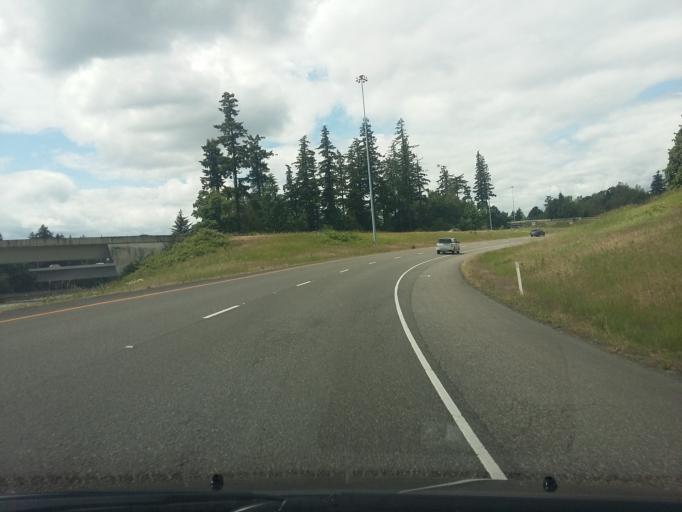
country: US
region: Washington
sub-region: Clark County
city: Orchards
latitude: 45.6032
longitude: -122.5472
